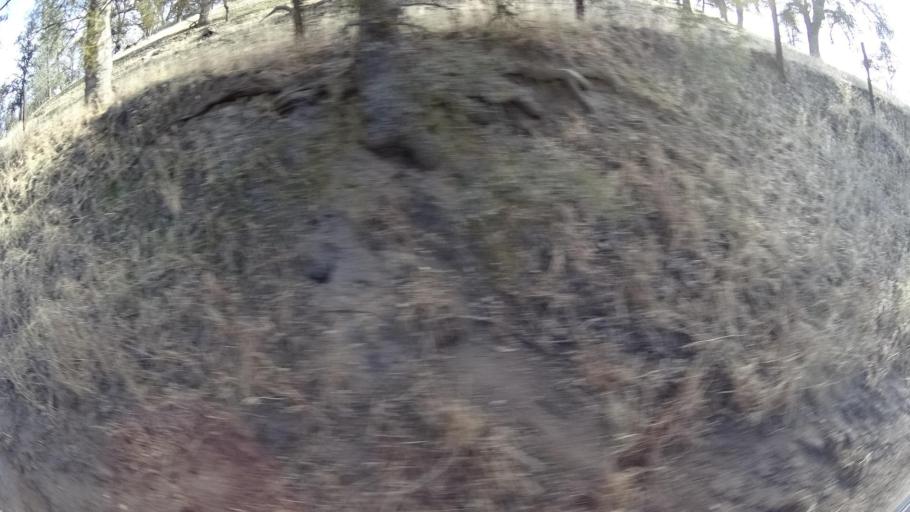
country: US
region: California
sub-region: Kern County
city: Alta Sierra
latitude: 35.6775
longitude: -118.7344
